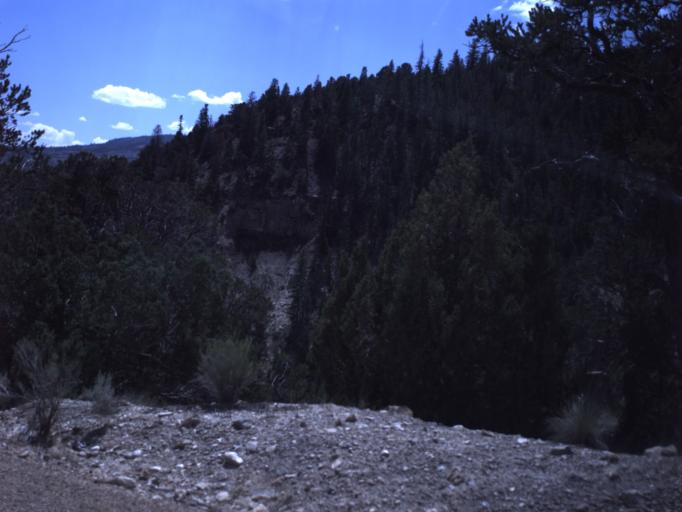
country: US
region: Utah
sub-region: Emery County
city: Orangeville
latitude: 39.2976
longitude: -111.3004
